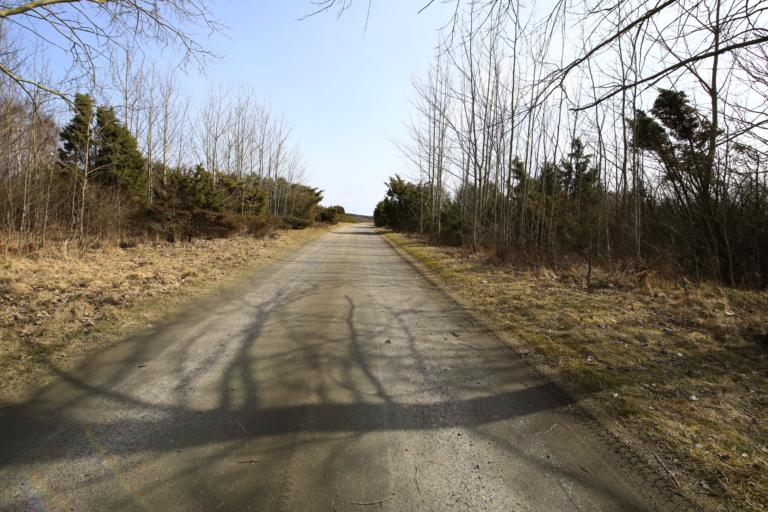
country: SE
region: Halland
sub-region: Kungsbacka Kommun
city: Frillesas
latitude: 57.2540
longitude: 12.1021
